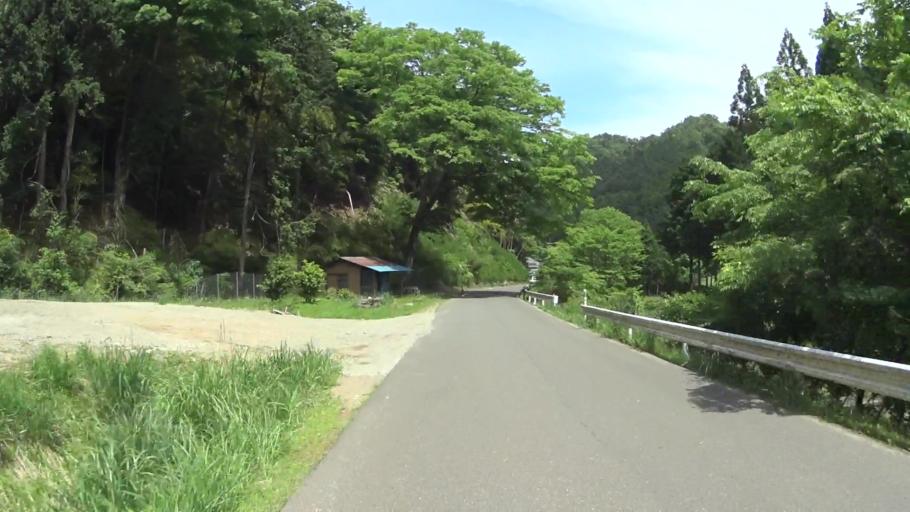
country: JP
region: Kyoto
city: Maizuru
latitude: 35.4392
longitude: 135.5146
